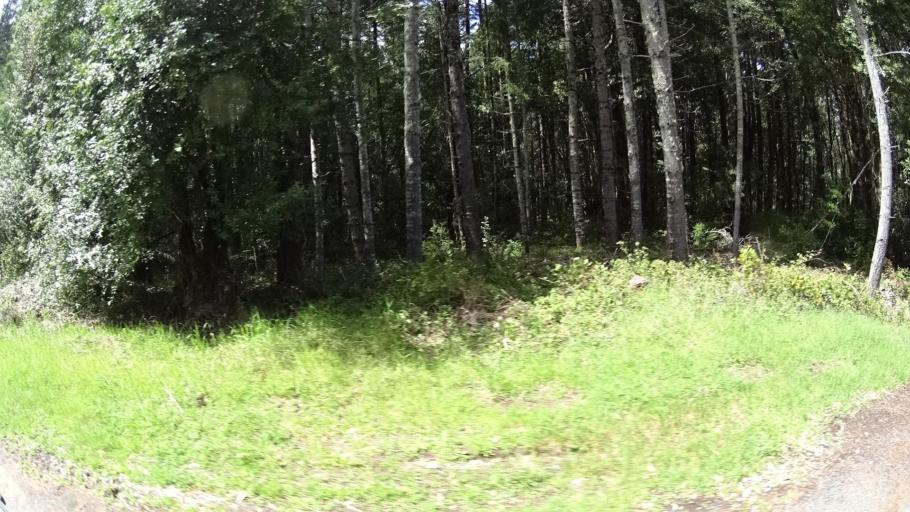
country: US
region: California
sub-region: Humboldt County
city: Blue Lake
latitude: 40.7598
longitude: -123.9650
